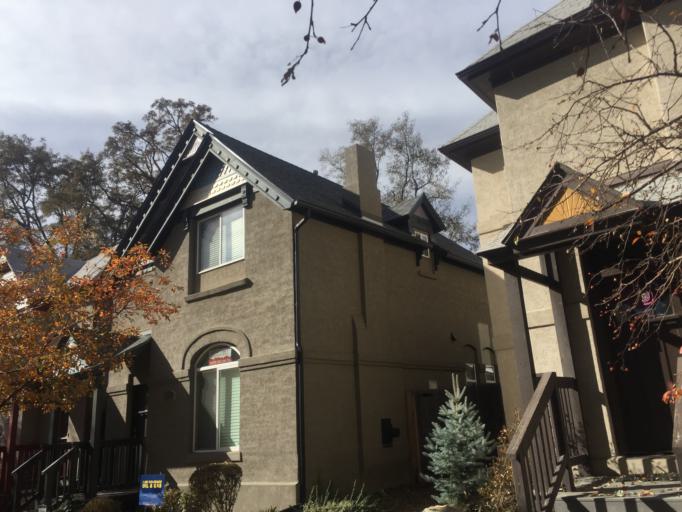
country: US
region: Colorado
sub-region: Denver County
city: Denver
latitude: 39.7492
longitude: -104.9747
